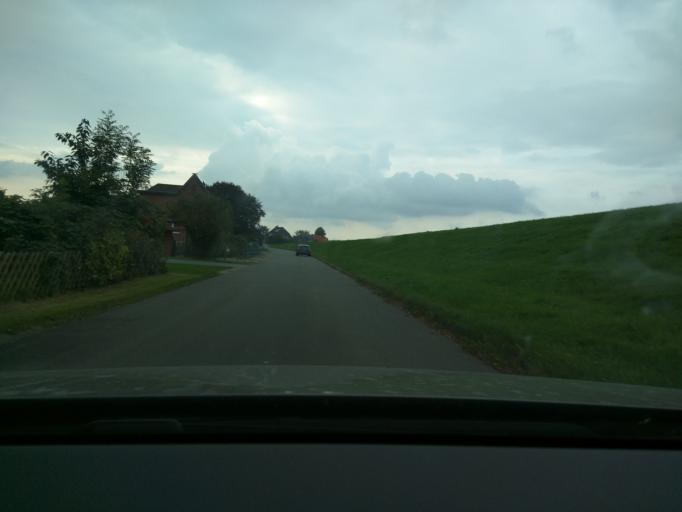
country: DE
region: Lower Saxony
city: Artlenburg
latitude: 53.3729
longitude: 10.4944
